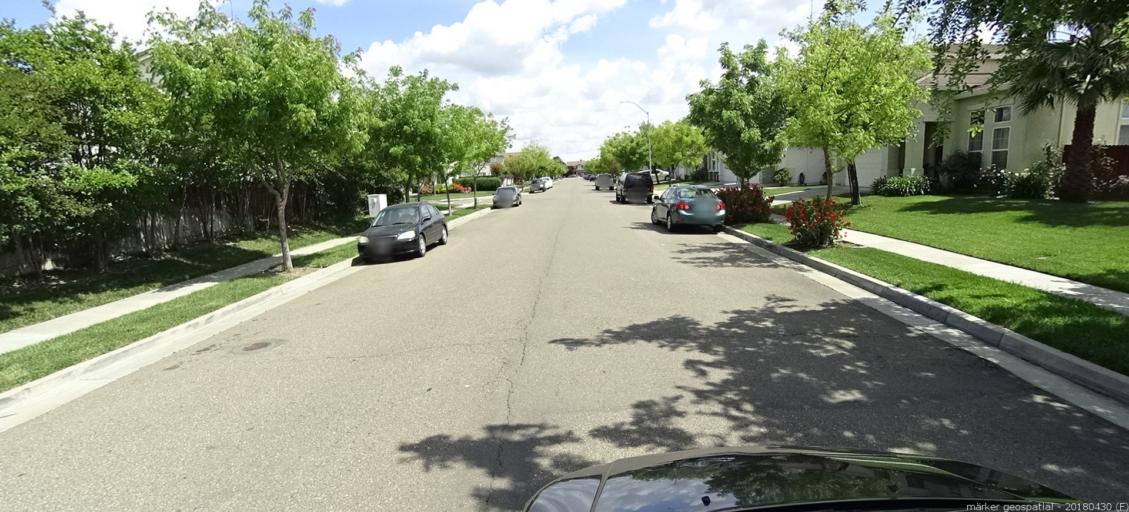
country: US
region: California
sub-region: Yolo County
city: West Sacramento
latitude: 38.5500
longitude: -121.5317
